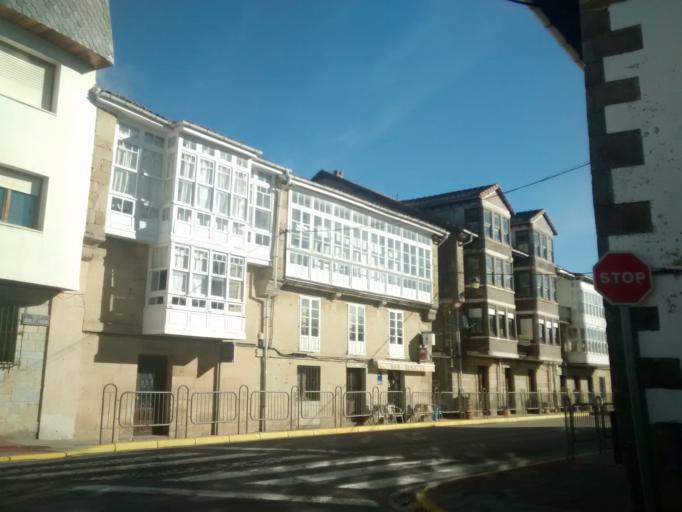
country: ES
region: Cantabria
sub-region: Provincia de Cantabria
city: San Pedro del Romeral
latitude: 42.9695
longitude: -3.7861
